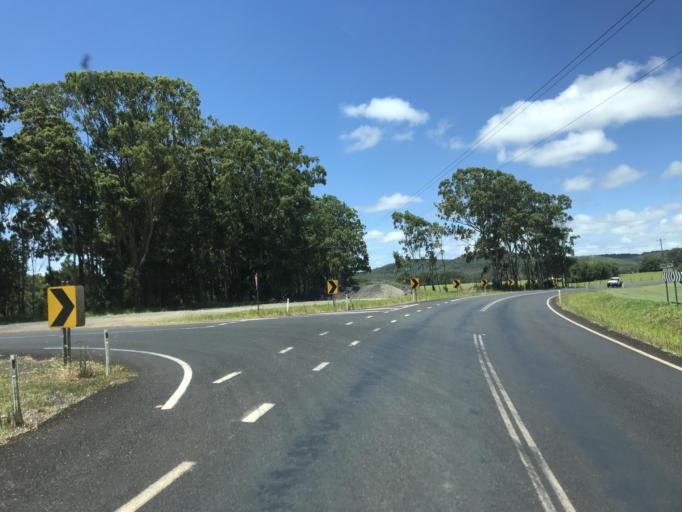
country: AU
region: Queensland
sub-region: Tablelands
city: Ravenshoe
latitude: -17.5148
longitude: 145.4503
